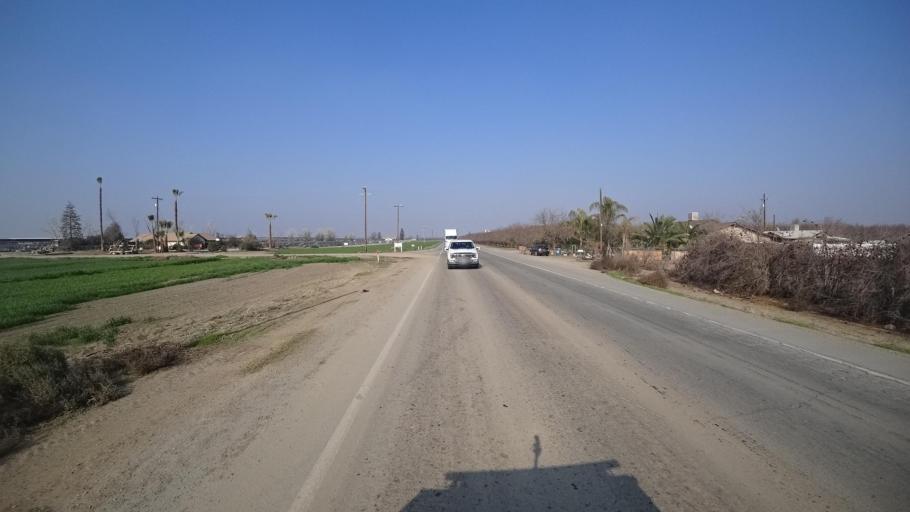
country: US
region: California
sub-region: Kern County
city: Greenfield
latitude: 35.2448
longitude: -119.1099
